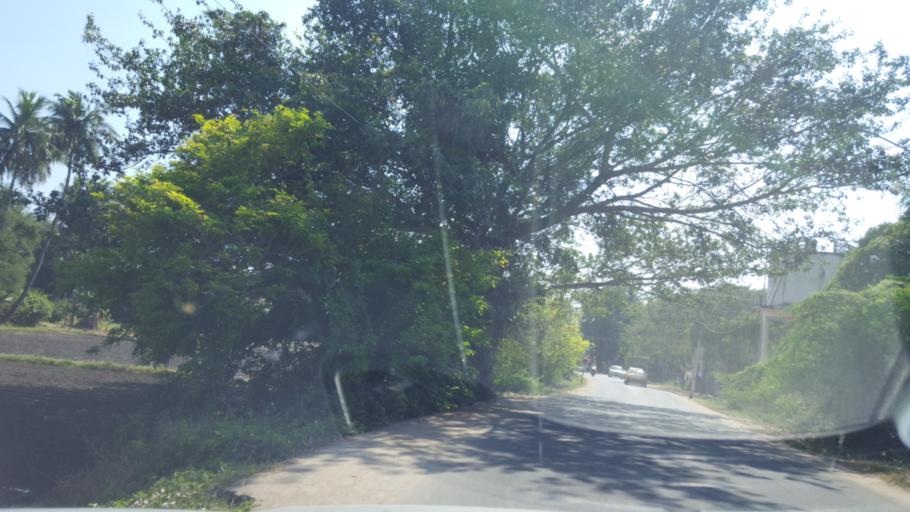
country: IN
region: Tamil Nadu
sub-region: Kancheepuram
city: Kanchipuram
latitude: 12.8416
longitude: 79.7437
